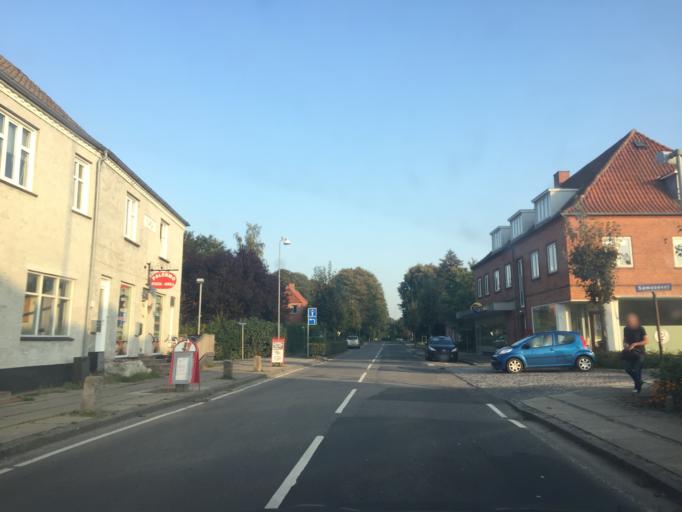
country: DK
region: Zealand
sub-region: Soro Kommune
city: Dianalund
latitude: 55.5326
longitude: 11.4974
